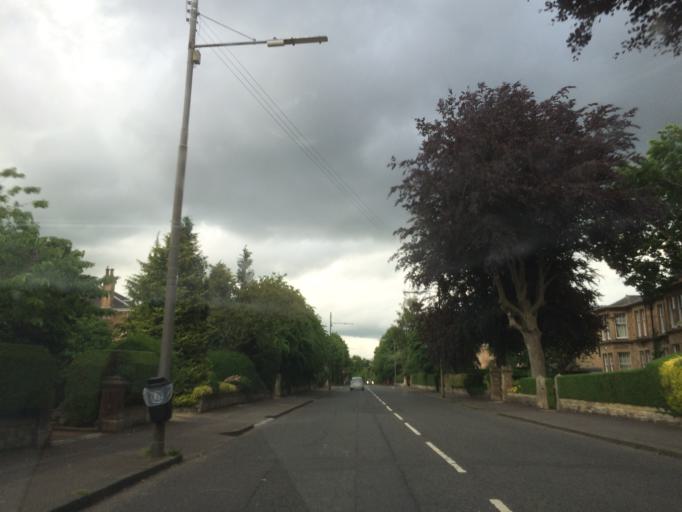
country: GB
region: Scotland
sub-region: East Renfrewshire
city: Giffnock
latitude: 55.8168
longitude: -4.2781
